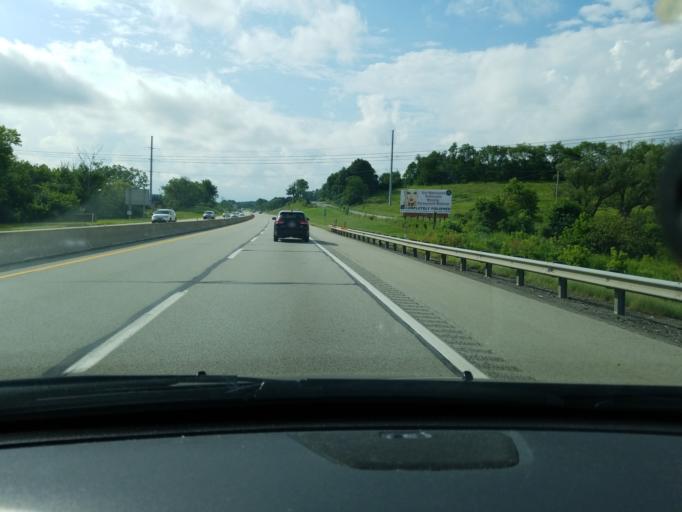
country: US
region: Pennsylvania
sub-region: Butler County
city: Fernway
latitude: 40.7082
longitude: -80.1254
